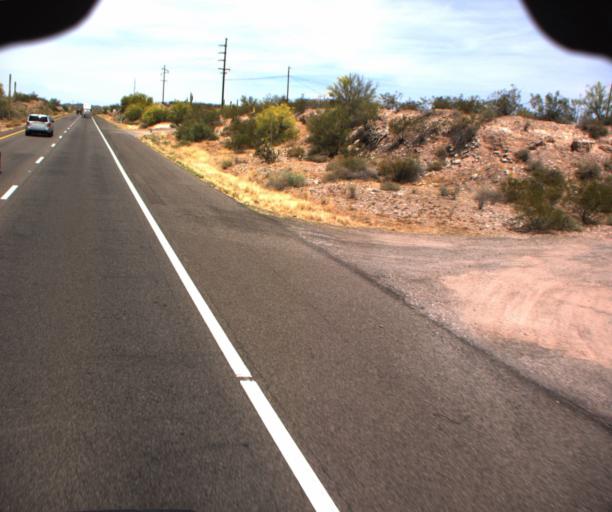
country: US
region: Arizona
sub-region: Maricopa County
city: Wickenburg
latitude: 33.8743
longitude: -112.6459
